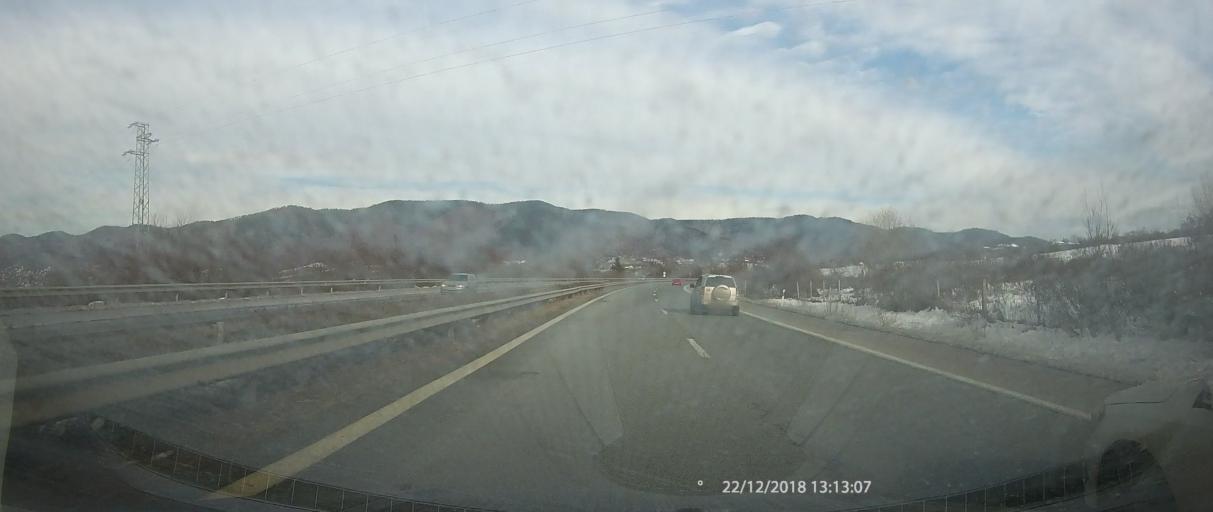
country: BG
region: Sofiya
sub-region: Obshtina Pravets
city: Pravets
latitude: 42.9021
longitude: 23.8609
